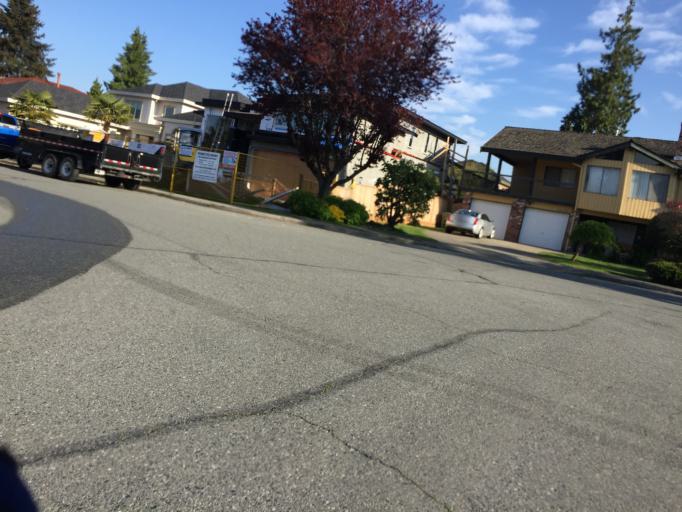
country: CA
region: British Columbia
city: Richmond
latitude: 49.1509
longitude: -123.1411
